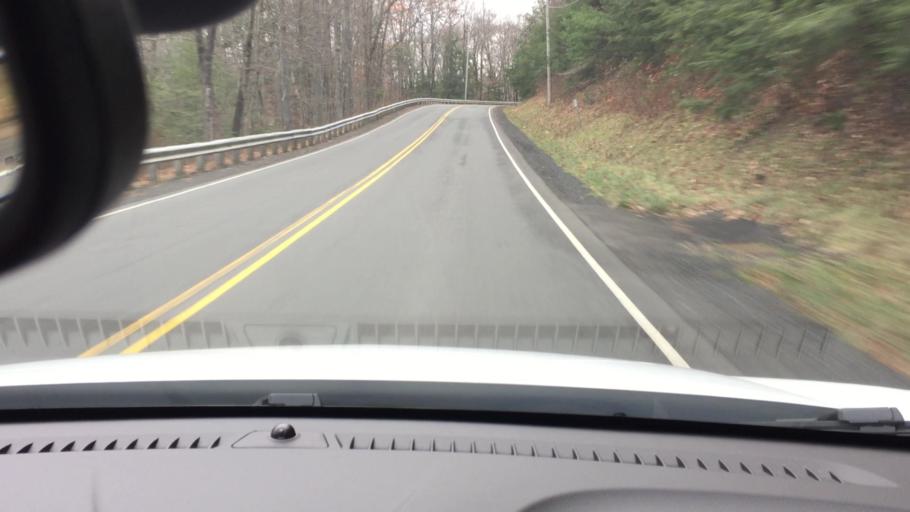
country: US
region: Massachusetts
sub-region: Berkshire County
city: New Marlborough
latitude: 42.1751
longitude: -73.1784
